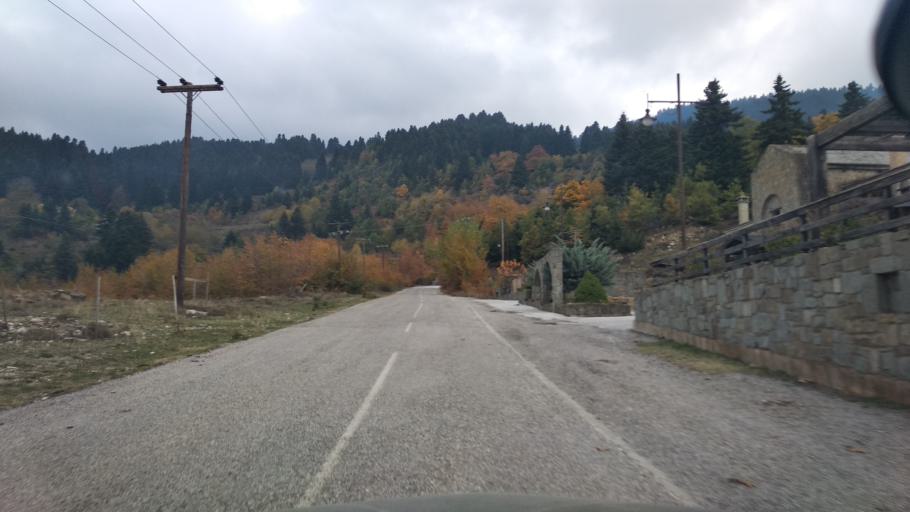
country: GR
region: Thessaly
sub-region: Trikala
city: Kalampaka
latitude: 39.5906
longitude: 21.4925
